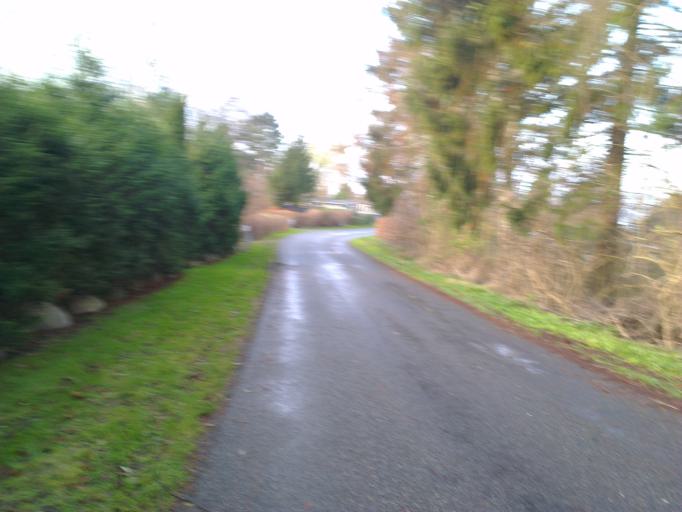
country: DK
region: Capital Region
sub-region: Frederikssund Kommune
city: Jaegerspris
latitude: 55.8393
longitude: 11.9665
